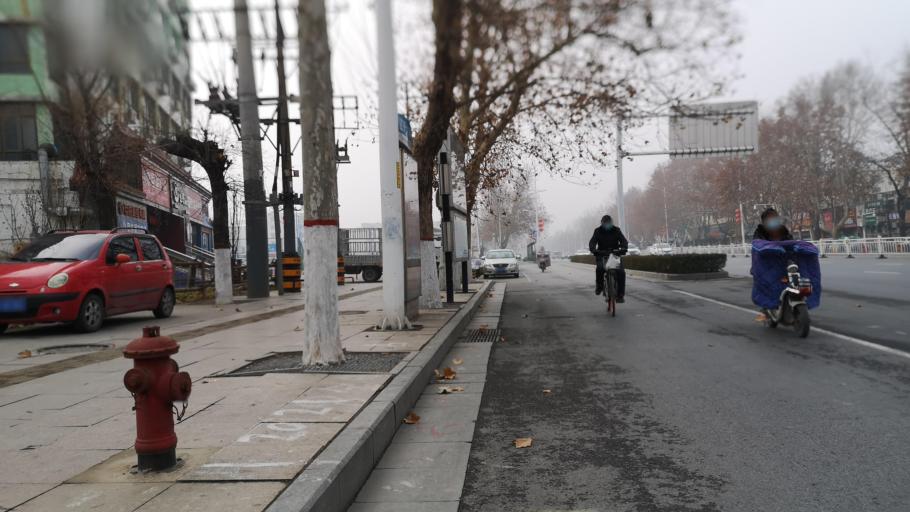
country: CN
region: Henan Sheng
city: Zhongyuanlu
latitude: 35.7795
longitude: 115.0435
